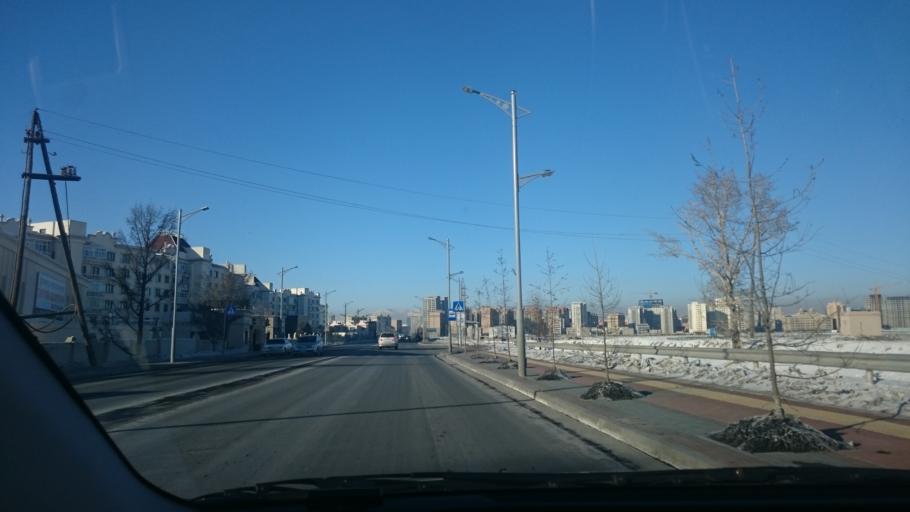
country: MN
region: Ulaanbaatar
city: Ulaanbaatar
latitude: 47.8921
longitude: 106.9374
